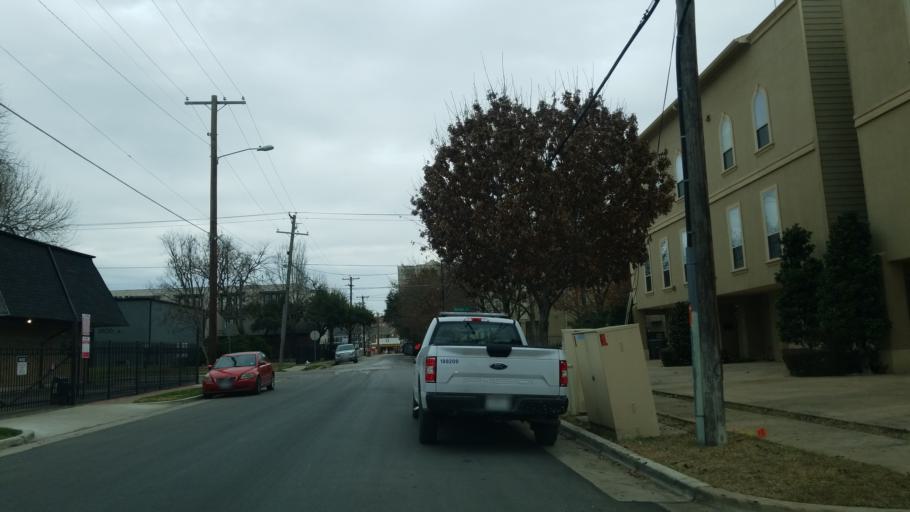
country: US
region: Texas
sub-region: Dallas County
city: Dallas
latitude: 32.8088
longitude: -96.8131
